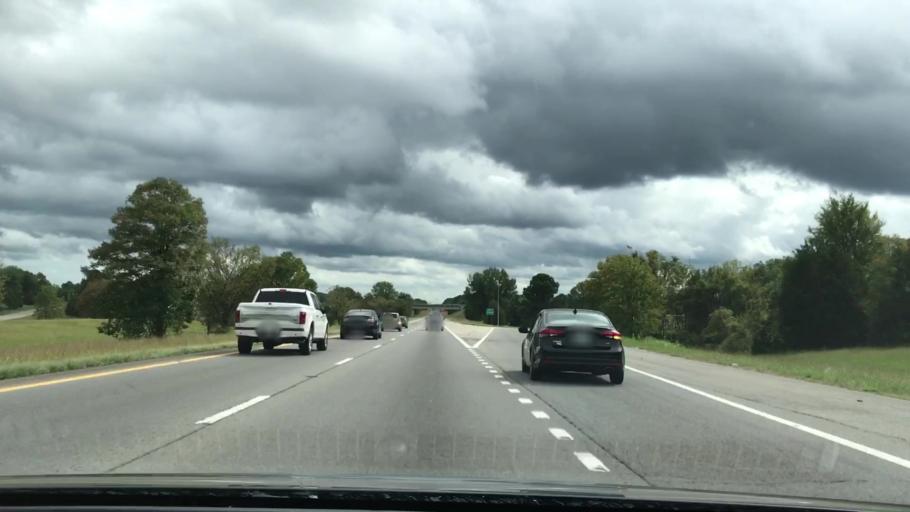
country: US
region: Tennessee
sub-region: Cheatham County
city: Pleasant View
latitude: 36.4049
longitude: -87.0310
